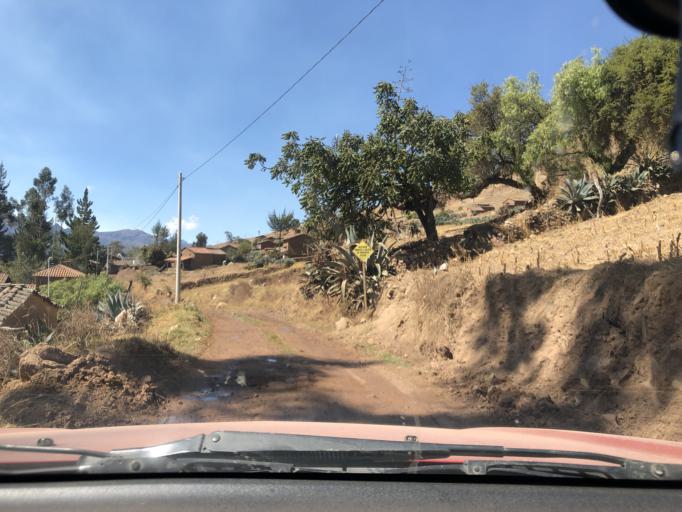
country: PE
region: Ayacucho
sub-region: Provincia de La Mar
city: Chilcas
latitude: -13.1691
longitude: -73.8489
